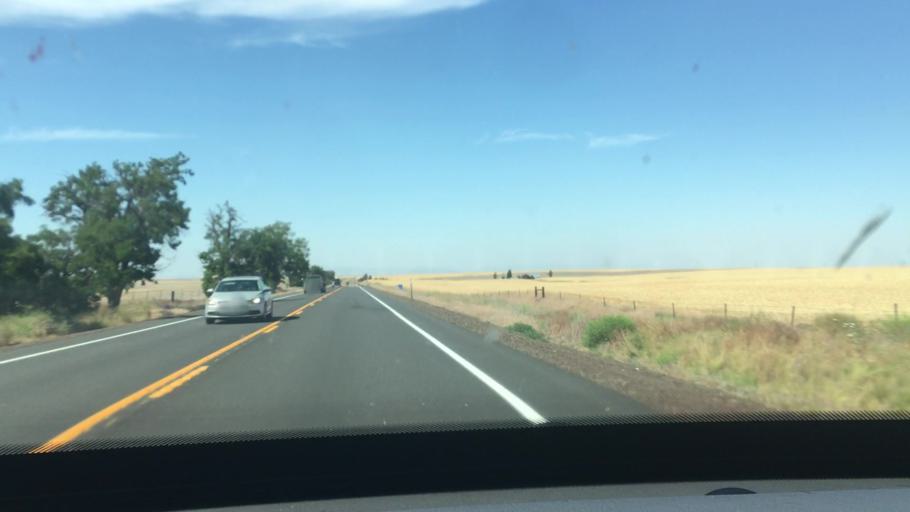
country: US
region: Oregon
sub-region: Sherman County
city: Moro
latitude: 45.3175
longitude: -120.7686
